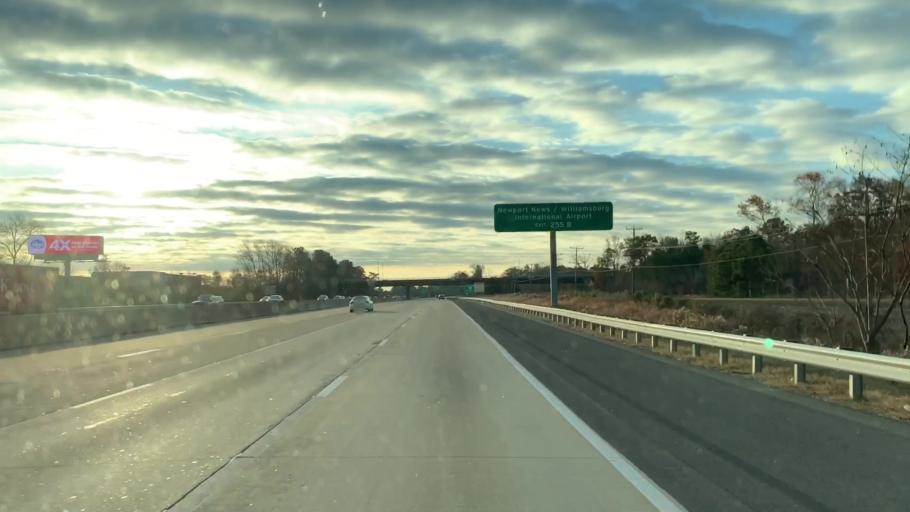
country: US
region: Virginia
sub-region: York County
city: Yorktown
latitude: 37.1276
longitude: -76.5201
